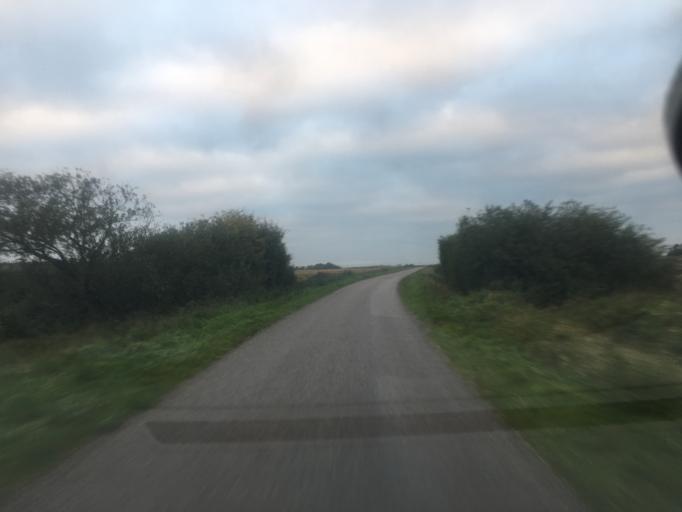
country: DK
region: South Denmark
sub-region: Tonder Kommune
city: Tonder
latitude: 54.9888
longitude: 8.9137
